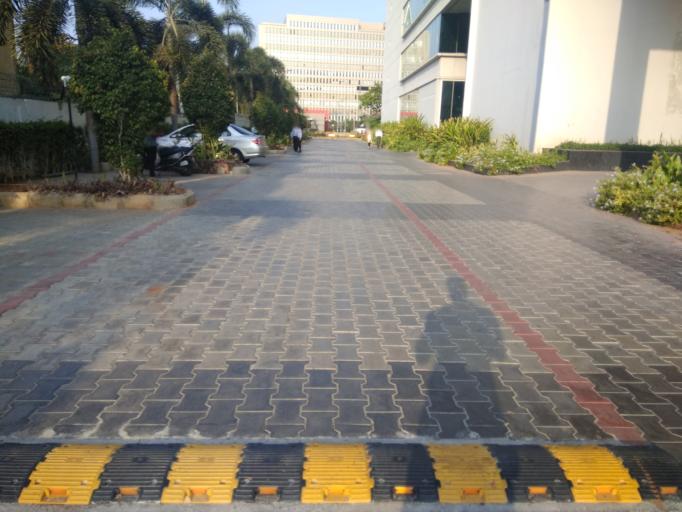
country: IN
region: Tamil Nadu
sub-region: Chennai
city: Gandhi Nagar
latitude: 12.9915
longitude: 80.2428
